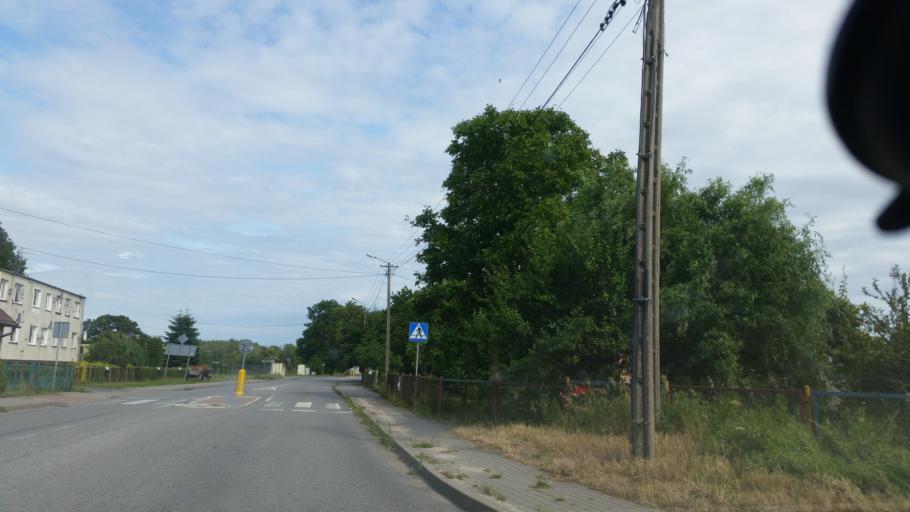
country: PL
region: Pomeranian Voivodeship
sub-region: Powiat wejherowski
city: Choczewo
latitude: 54.7251
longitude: 17.8561
